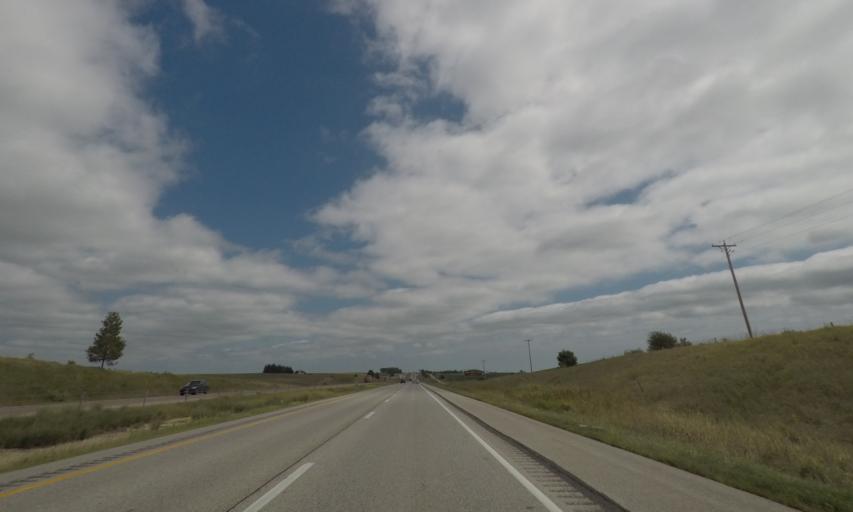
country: US
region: Iowa
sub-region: Iowa County
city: Marengo
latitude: 41.6961
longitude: -92.1817
